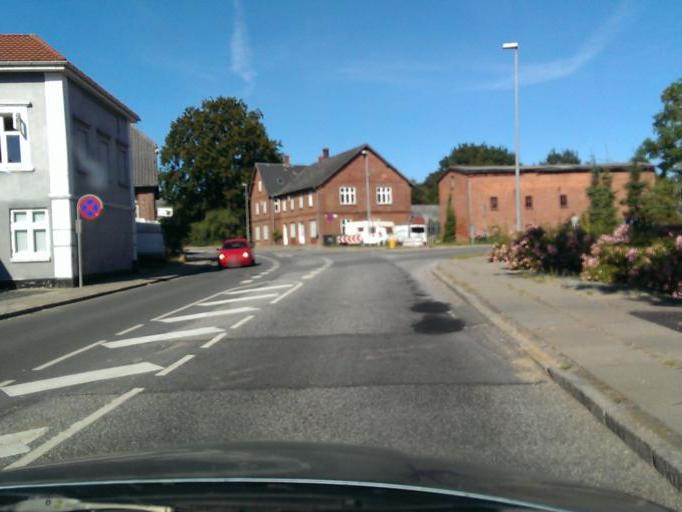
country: DK
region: Central Jutland
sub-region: Odder Kommune
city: Odder
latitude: 55.9260
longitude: 10.1535
